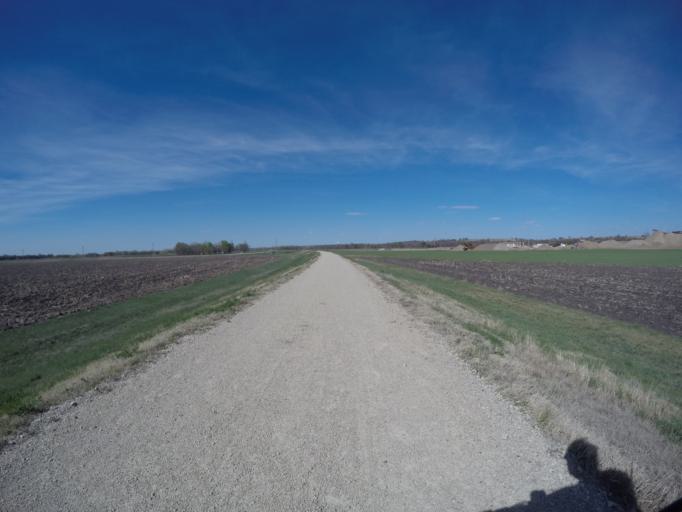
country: US
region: Kansas
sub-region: Saline County
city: Salina
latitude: 38.7814
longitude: -97.5766
